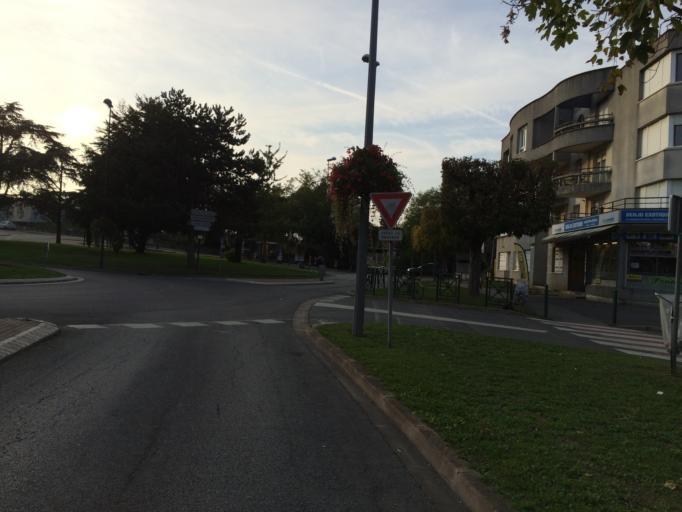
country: FR
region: Ile-de-France
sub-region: Departement de l'Essonne
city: Vigneux-sur-Seine
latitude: 48.7084
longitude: 2.4165
